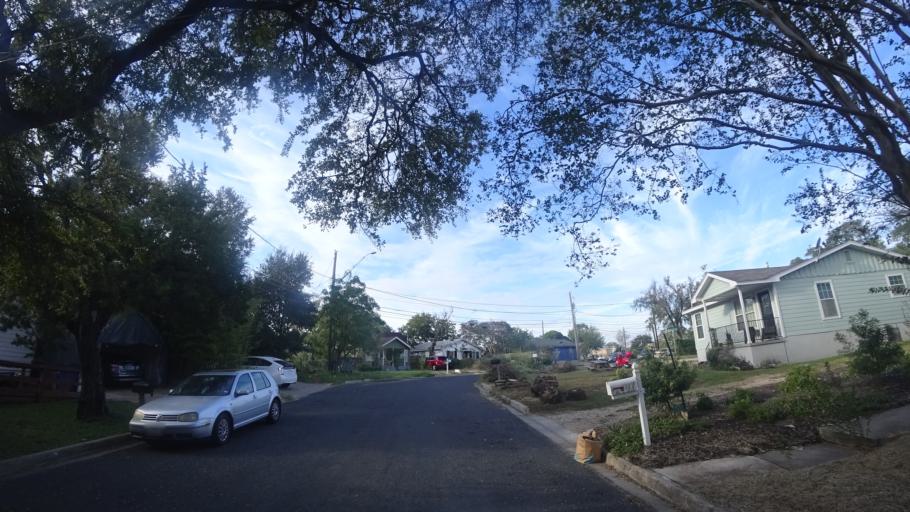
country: US
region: Texas
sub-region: Travis County
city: Austin
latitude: 30.2733
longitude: -97.7072
